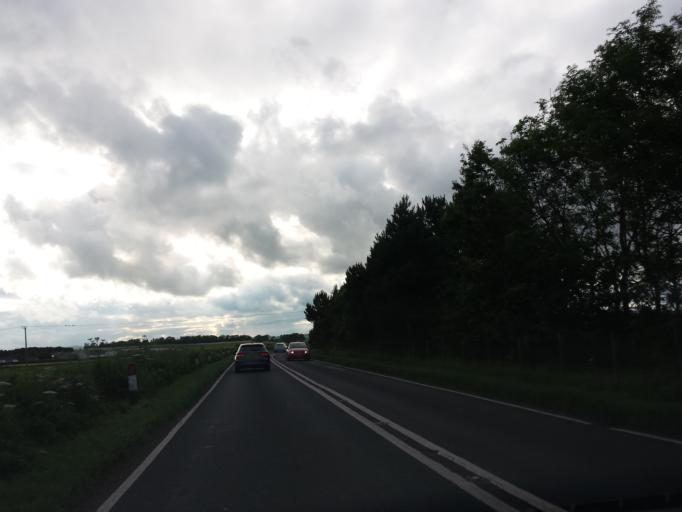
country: GB
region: Scotland
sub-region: Fife
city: Strathkinness
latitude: 56.3500
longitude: -2.8377
